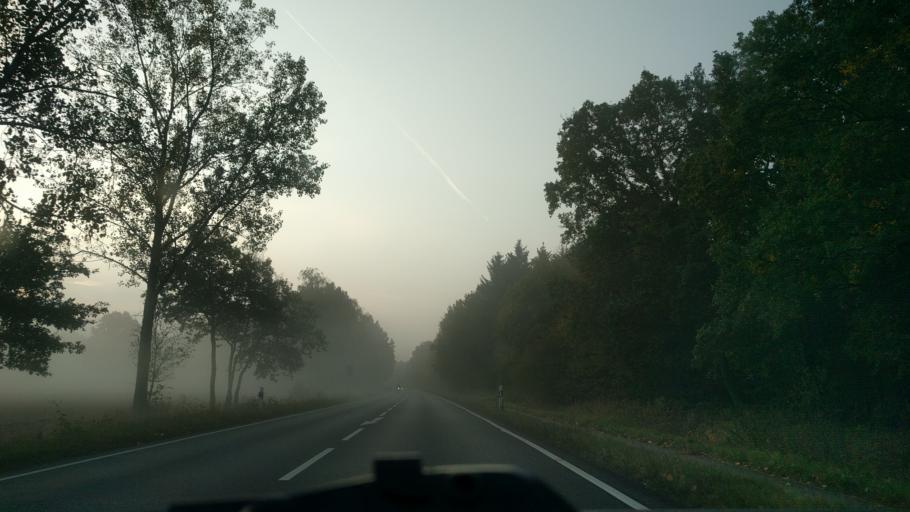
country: DE
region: Lower Saxony
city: Isenbuttel
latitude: 52.4485
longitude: 10.5881
